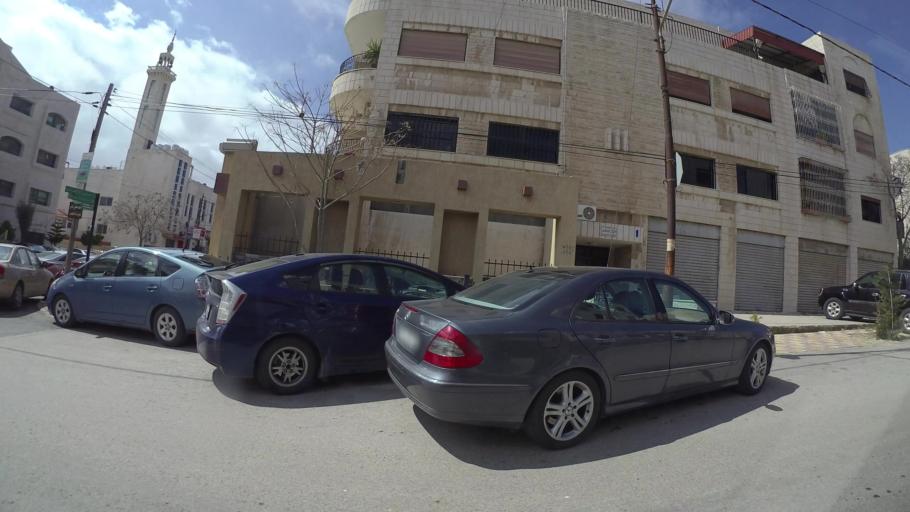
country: JO
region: Amman
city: Wadi as Sir
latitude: 31.9553
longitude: 35.8394
